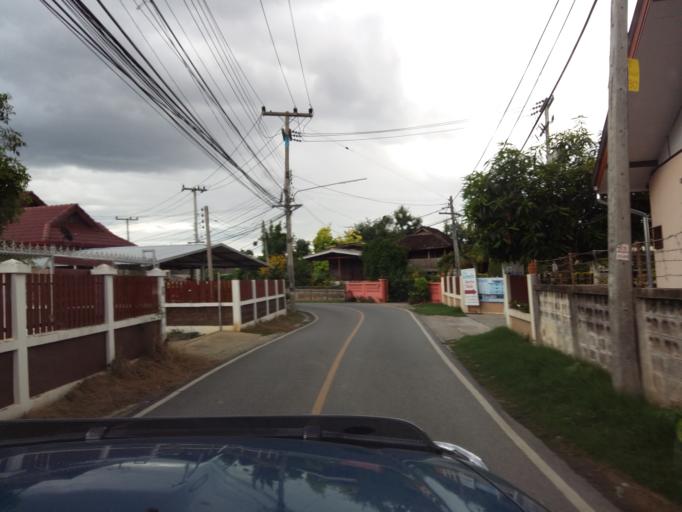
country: TH
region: Chiang Mai
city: Chiang Mai
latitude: 18.7412
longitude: 98.9490
